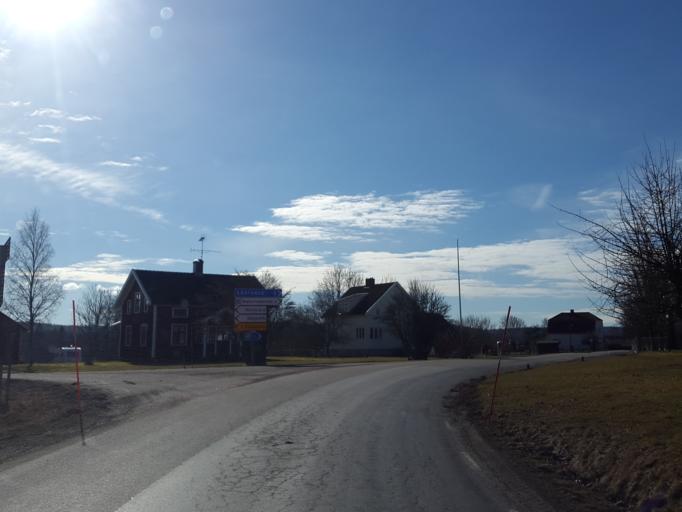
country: SE
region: Vaestra Goetaland
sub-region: Vargarda Kommun
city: Jonstorp
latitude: 57.9681
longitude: 12.7280
